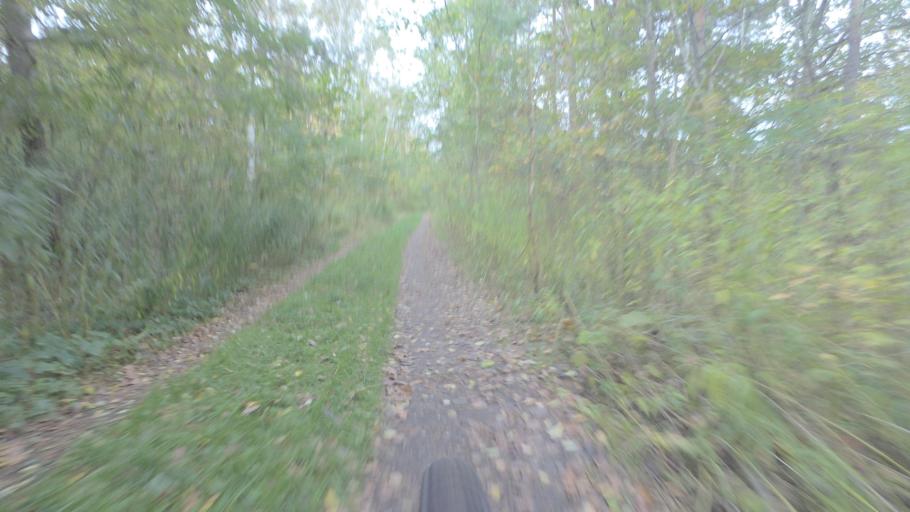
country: DE
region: Brandenburg
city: Ludwigsfelde
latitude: 52.3118
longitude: 13.2703
